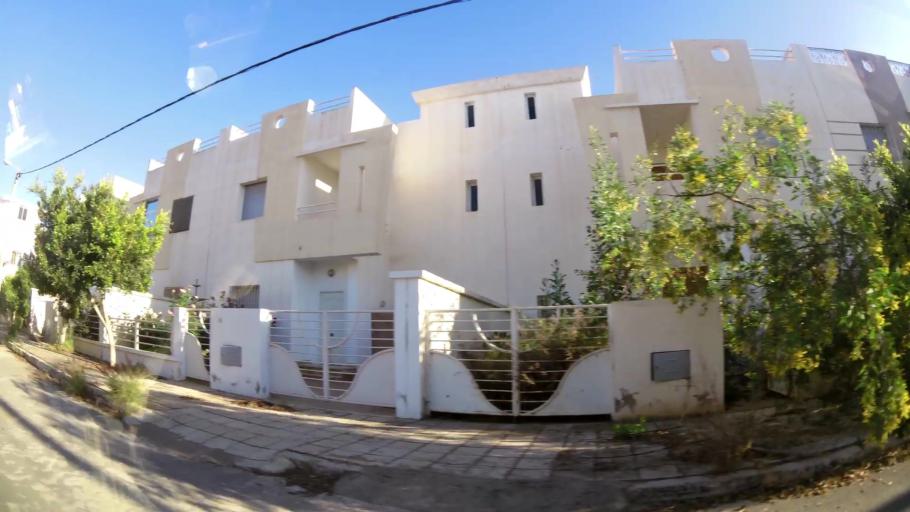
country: MA
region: Oriental
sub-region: Berkane-Taourirt
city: Madagh
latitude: 35.0843
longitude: -2.2496
